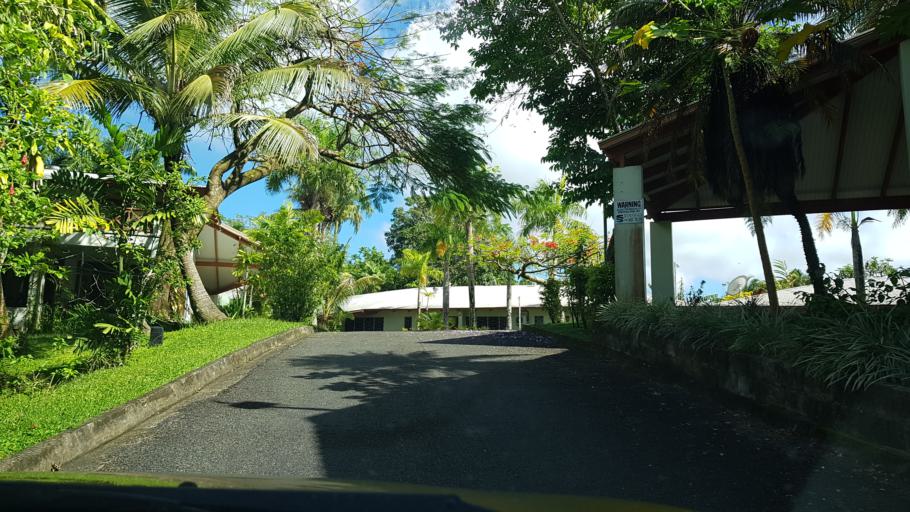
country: FJ
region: Central
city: Suva
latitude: -18.1509
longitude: 178.4408
